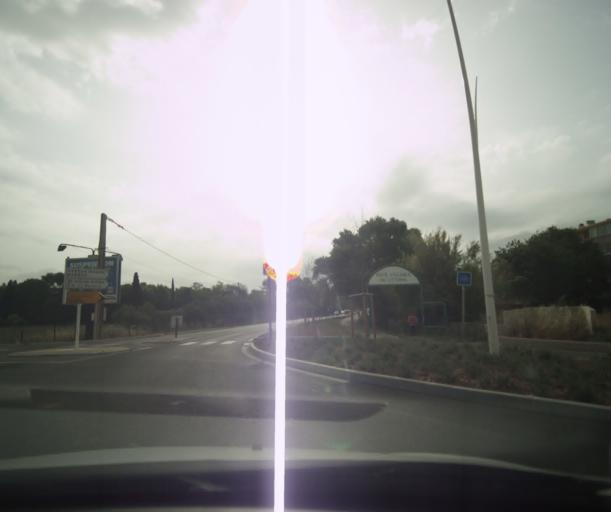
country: FR
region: Provence-Alpes-Cote d'Azur
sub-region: Departement du Var
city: Le Pradet
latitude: 43.1108
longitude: 6.0166
